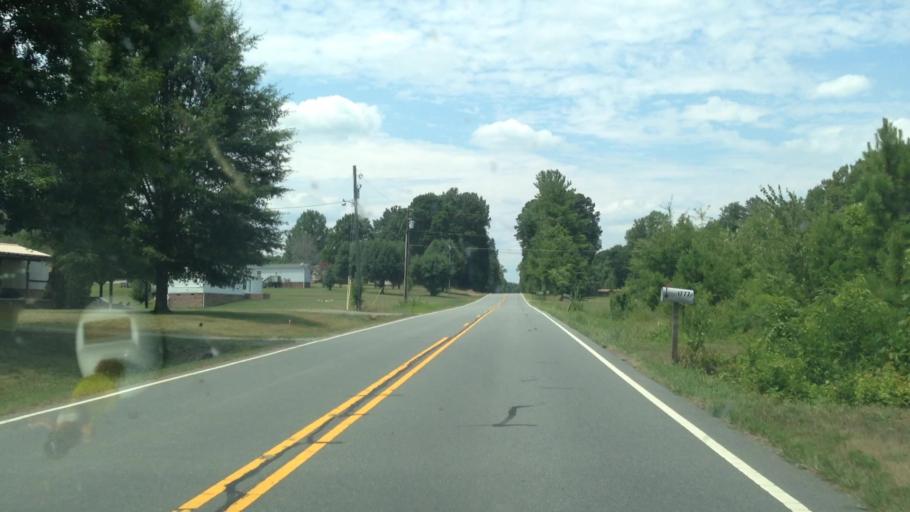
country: US
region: North Carolina
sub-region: Stokes County
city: Walnut Cove
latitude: 36.3605
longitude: -80.0639
